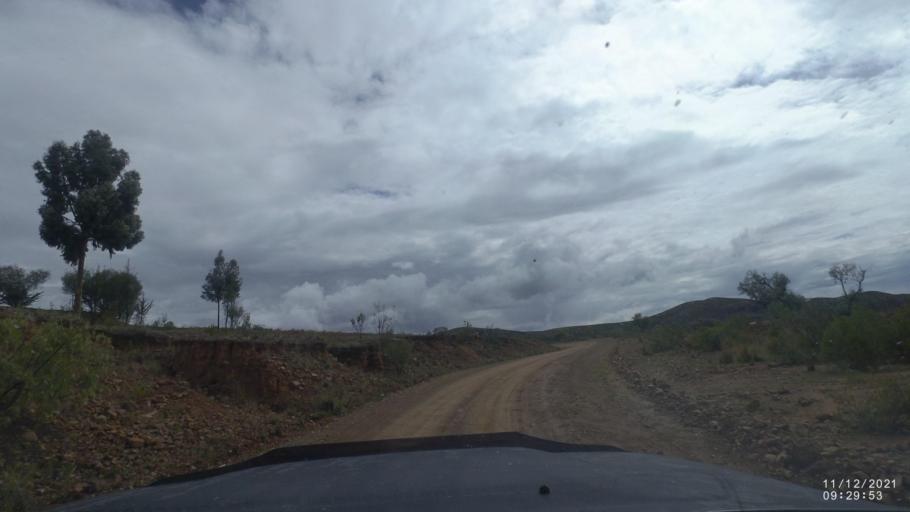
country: BO
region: Cochabamba
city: Tarata
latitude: -17.8619
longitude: -65.9887
